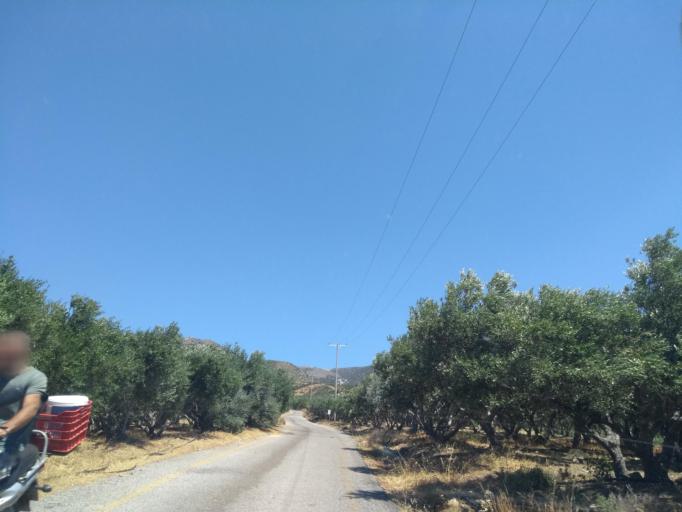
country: GR
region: Crete
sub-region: Nomos Chanias
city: Vryses
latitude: 35.3616
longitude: 23.5374
